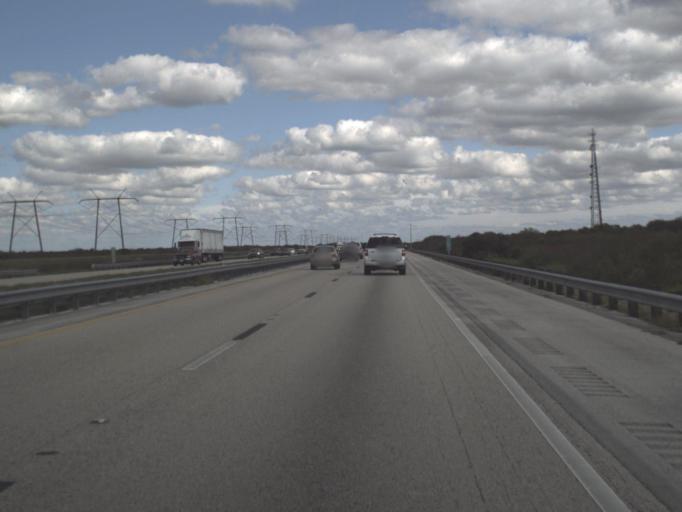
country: US
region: Florida
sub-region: Indian River County
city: West Vero Corridor
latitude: 27.5593
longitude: -80.7037
